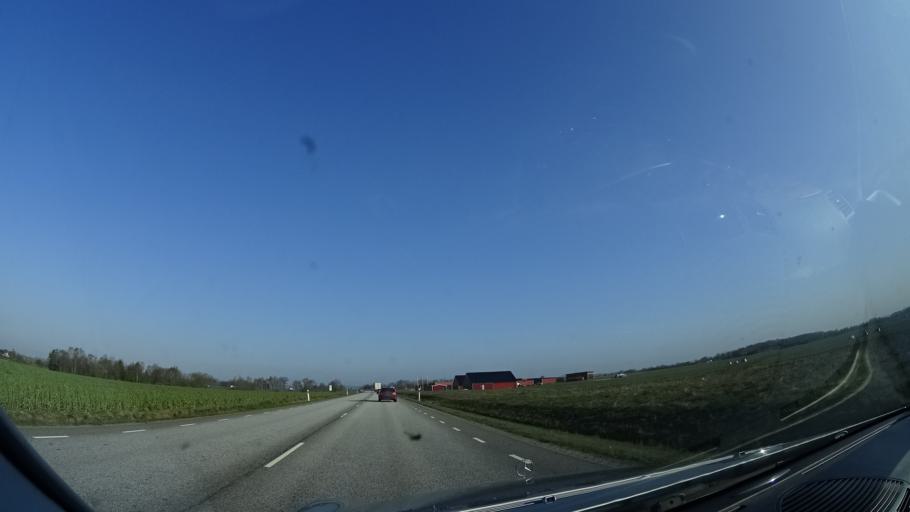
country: SE
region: Skane
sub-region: Eslovs Kommun
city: Eslov
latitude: 55.8460
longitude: 13.3241
